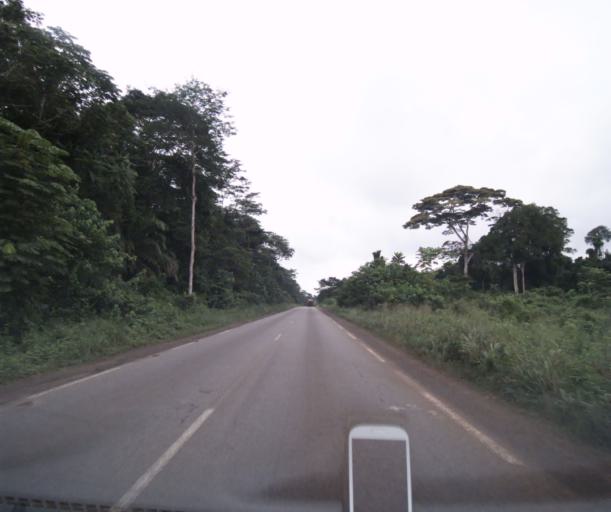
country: CM
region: Littoral
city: Edea
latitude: 3.8133
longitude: 10.3143
